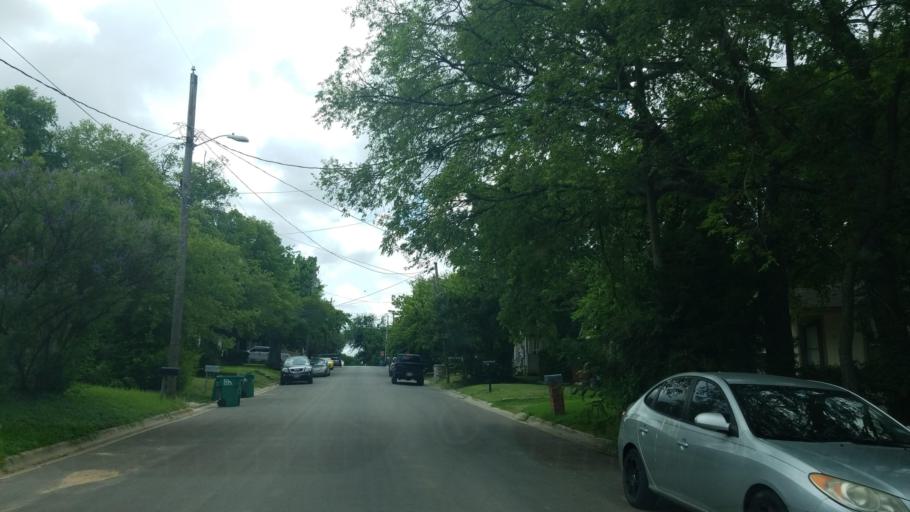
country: US
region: Texas
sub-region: Denton County
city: Denton
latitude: 33.2035
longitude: -97.1436
